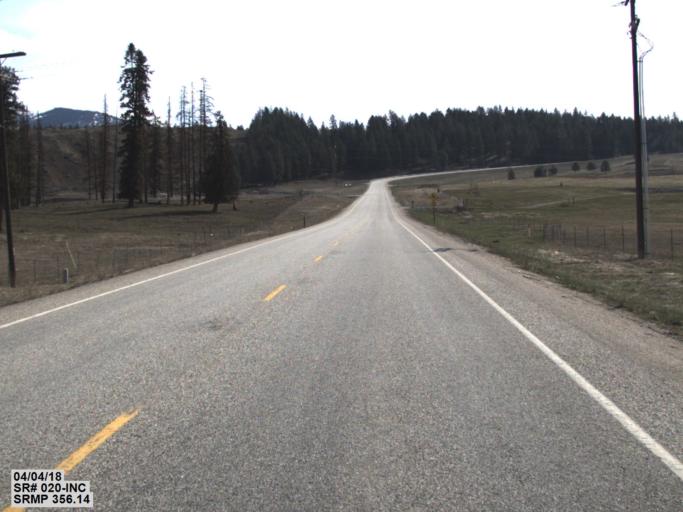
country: US
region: Washington
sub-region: Stevens County
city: Colville
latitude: 48.5474
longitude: -117.8672
